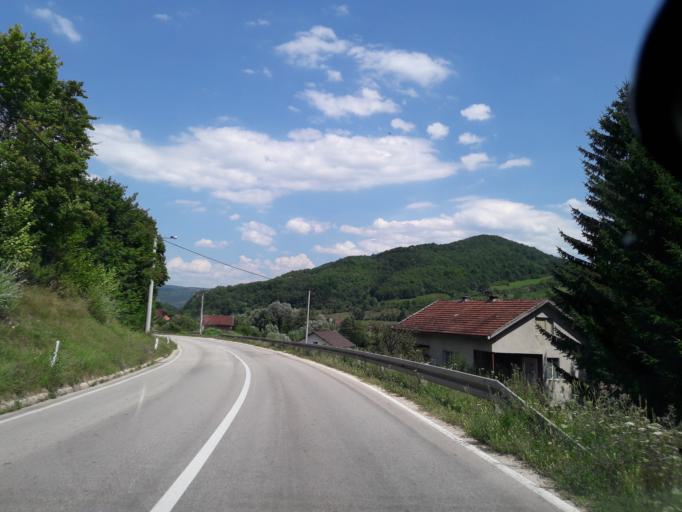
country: BA
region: Republika Srpska
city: Mrkonjic Grad
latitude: 44.4210
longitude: 17.1129
